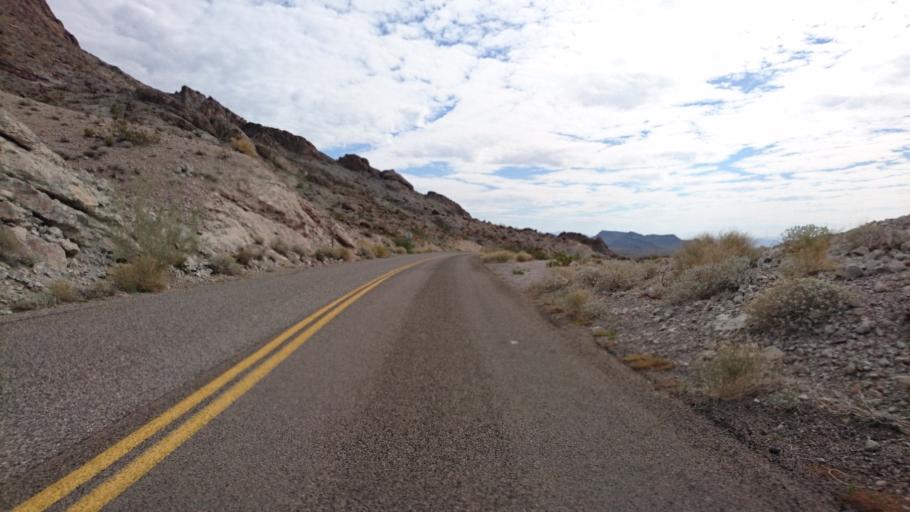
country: US
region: Arizona
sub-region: Mohave County
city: Mohave Valley
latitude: 34.9844
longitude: -114.4248
